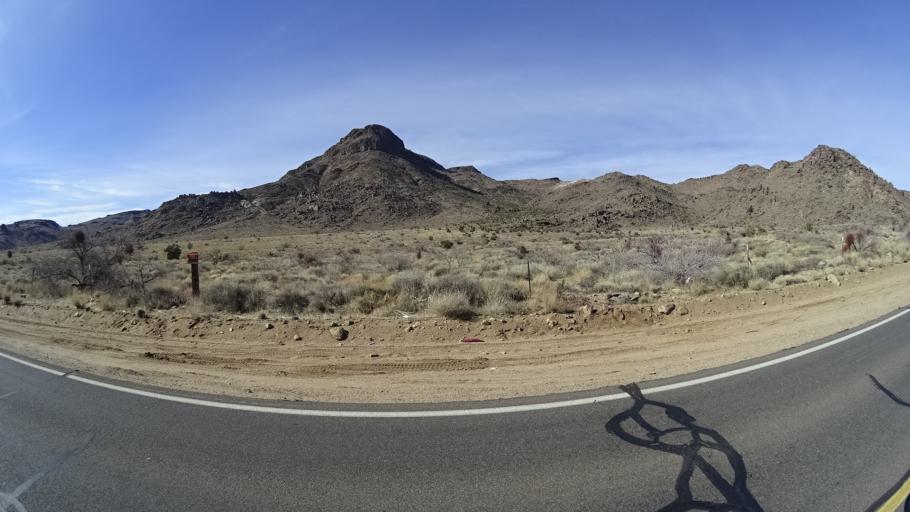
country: US
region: Arizona
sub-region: Mohave County
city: New Kingman-Butler
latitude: 35.2841
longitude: -114.0542
